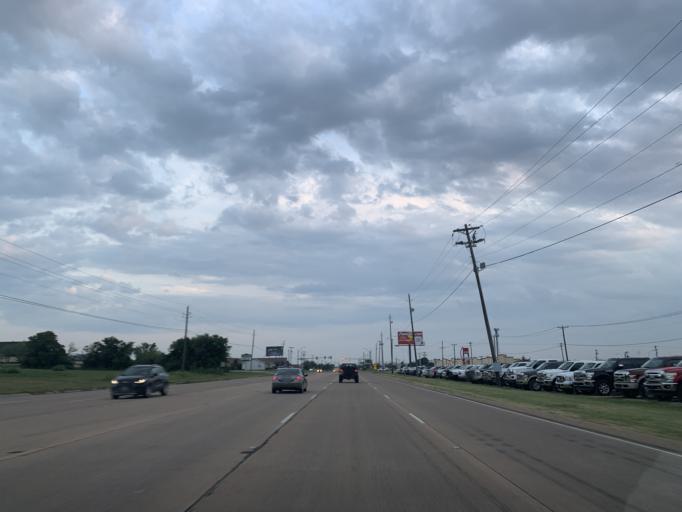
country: US
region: Texas
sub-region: Tarrant County
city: Keller
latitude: 32.9136
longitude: -97.2557
